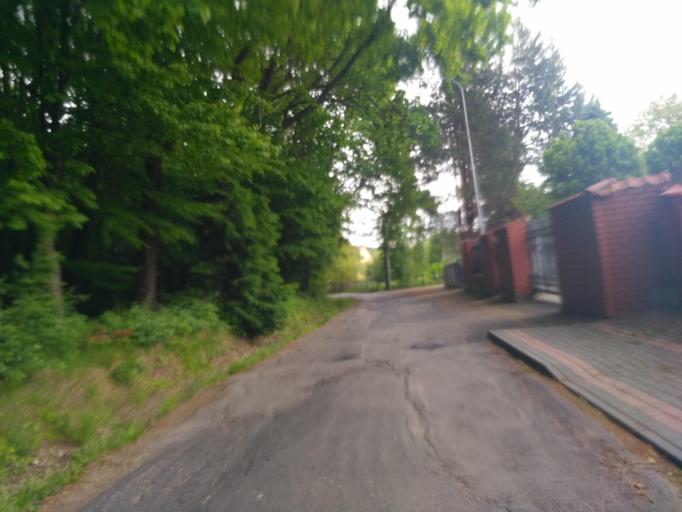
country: PL
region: Subcarpathian Voivodeship
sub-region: Powiat krosnienski
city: Odrzykon
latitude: 49.7240
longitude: 21.7101
